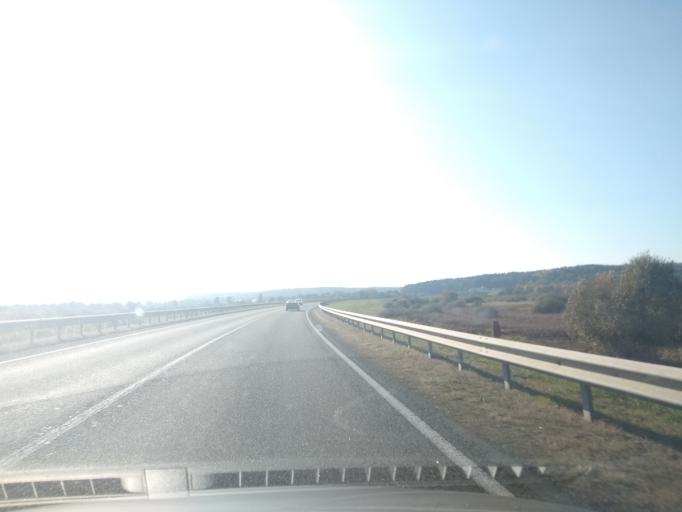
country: BY
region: Grodnenskaya
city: Zhyrovichy
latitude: 53.0493
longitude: 25.3719
